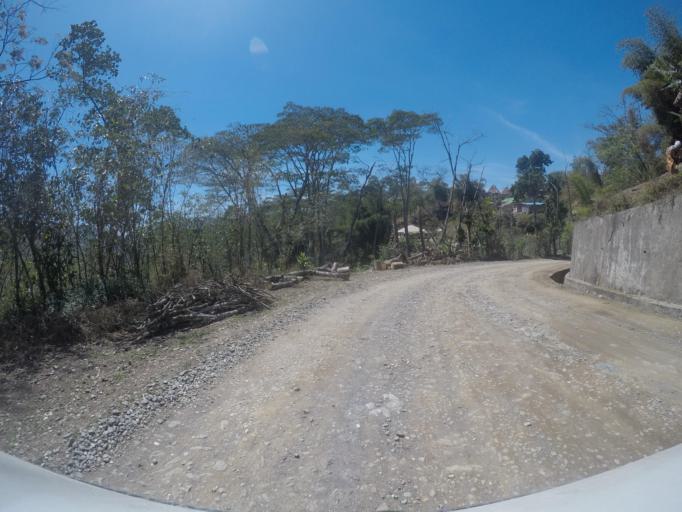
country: TL
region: Ermera
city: Gleno
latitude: -8.7821
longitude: 125.3754
